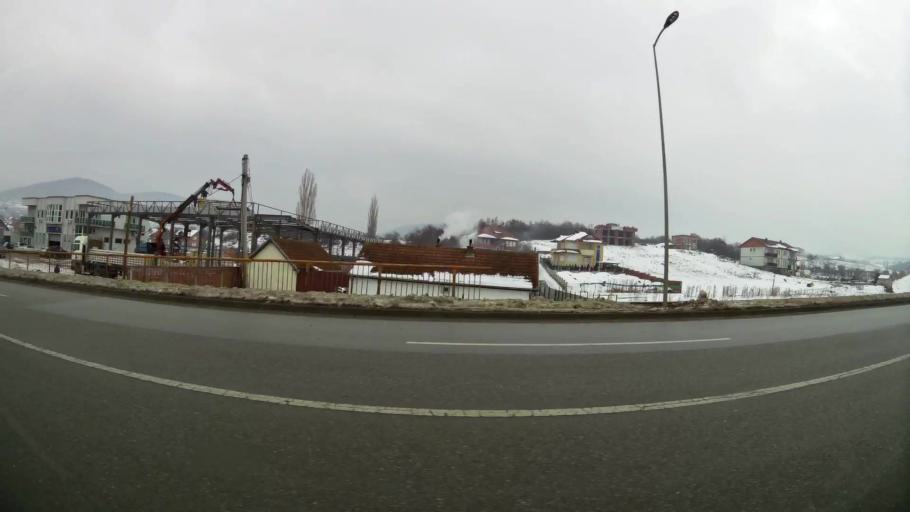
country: XK
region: Pristina
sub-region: Komuna e Prishtines
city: Pristina
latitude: 42.7068
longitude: 21.1545
